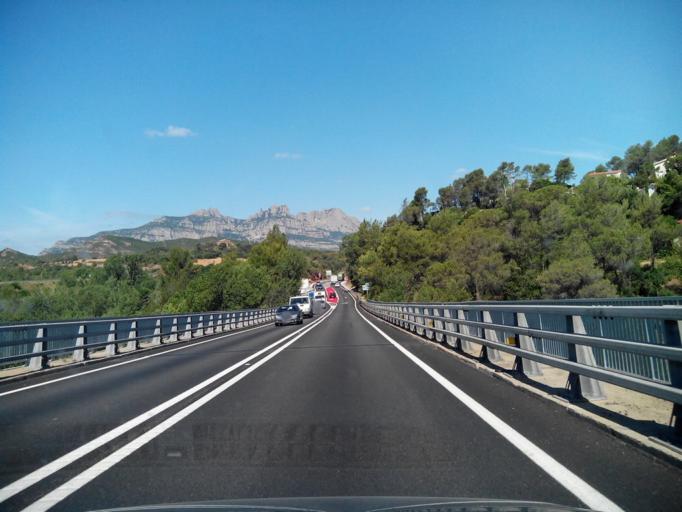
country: ES
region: Catalonia
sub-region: Provincia de Barcelona
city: Viladecavalls
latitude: 41.5858
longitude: 1.9229
